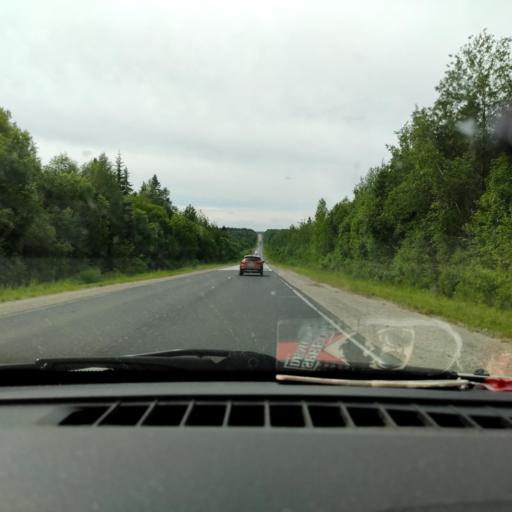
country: RU
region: Perm
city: Chusovoy
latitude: 58.3726
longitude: 57.9972
